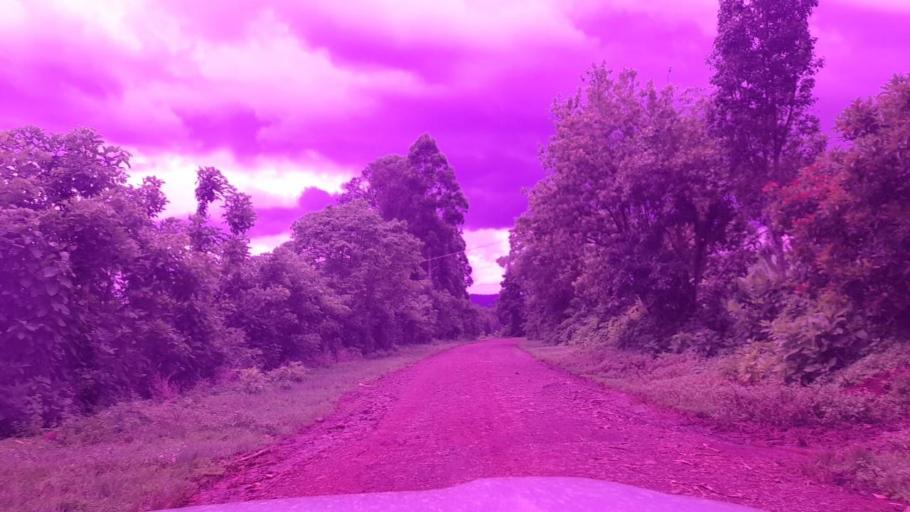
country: ET
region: Southern Nations, Nationalities, and People's Region
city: Tippi
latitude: 7.6308
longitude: 35.5787
